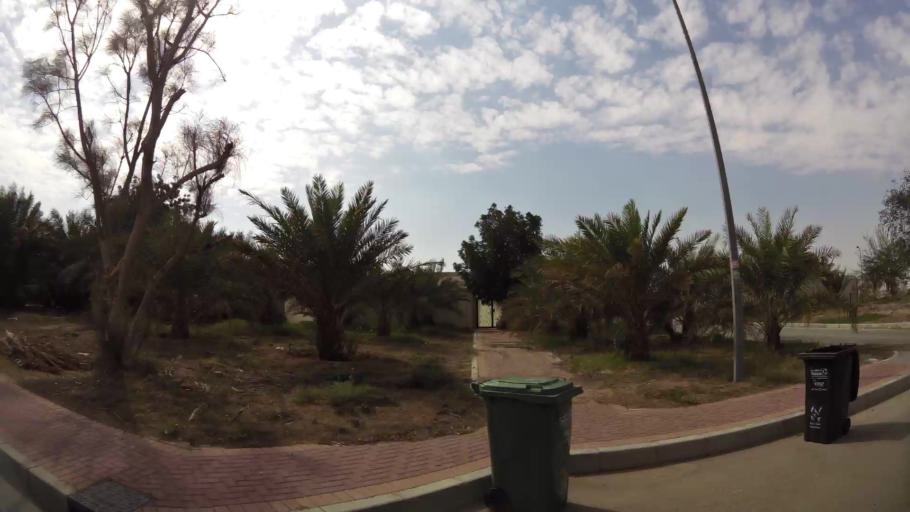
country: AE
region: Abu Dhabi
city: Al Ain
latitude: 24.1015
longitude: 55.8988
